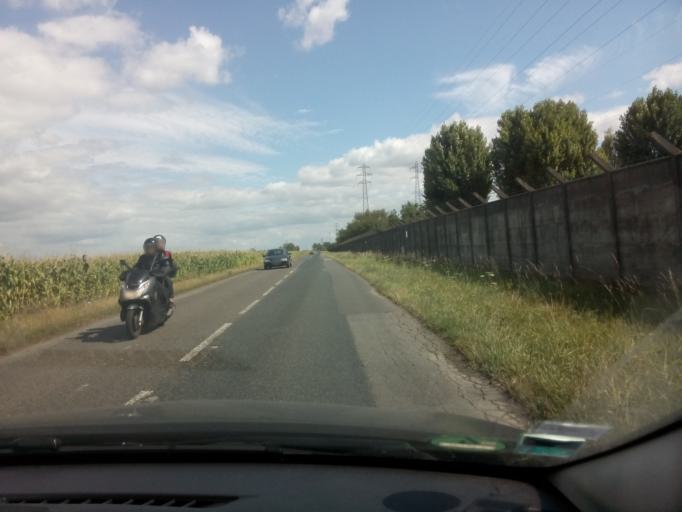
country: FR
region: Ile-de-France
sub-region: Departement des Yvelines
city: Jouy-en-Josas
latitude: 48.7481
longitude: 2.1760
